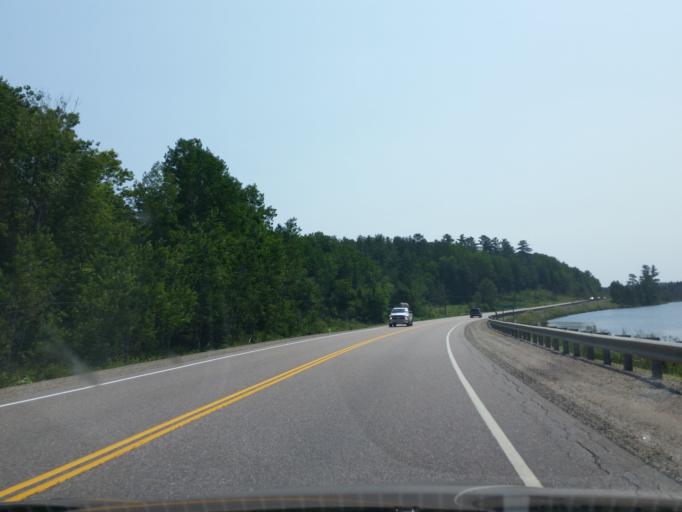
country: CA
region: Ontario
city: Deep River
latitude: 46.1808
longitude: -77.7261
